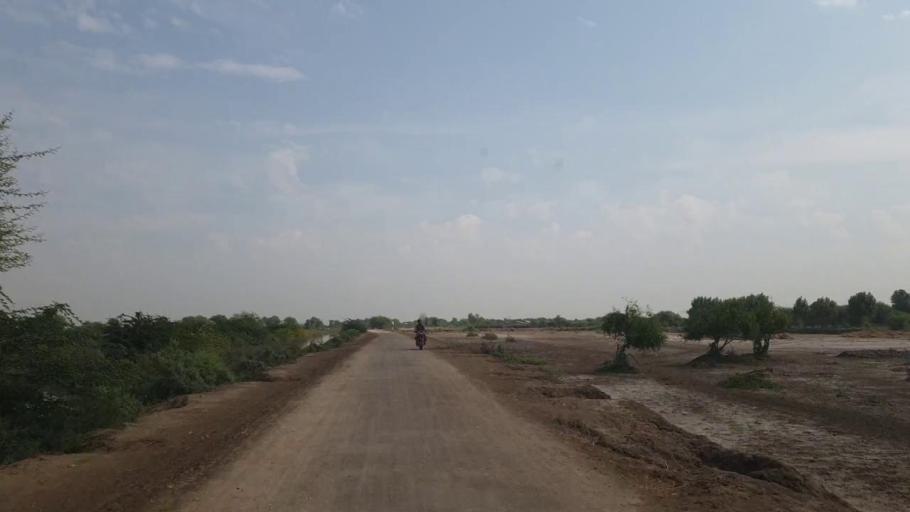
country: PK
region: Sindh
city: Rajo Khanani
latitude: 24.9563
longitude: 69.0150
